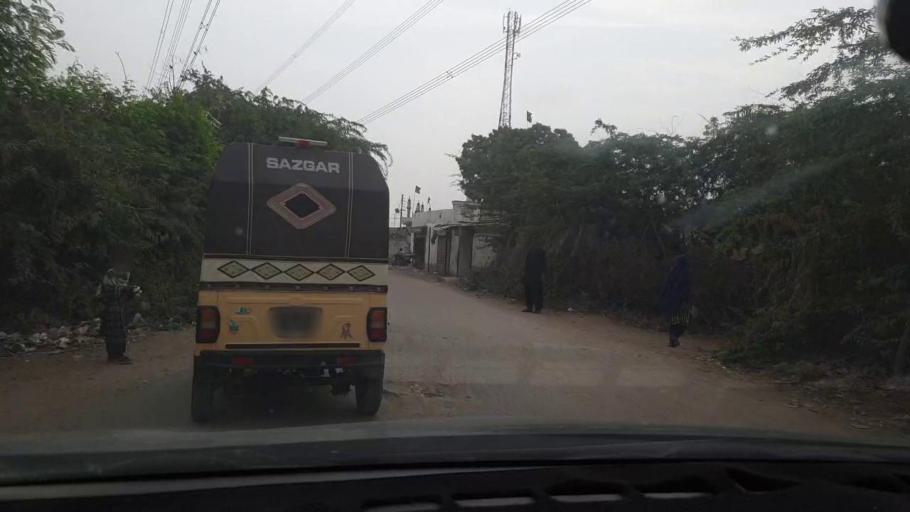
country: PK
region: Sindh
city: Malir Cantonment
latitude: 24.9074
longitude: 67.2858
